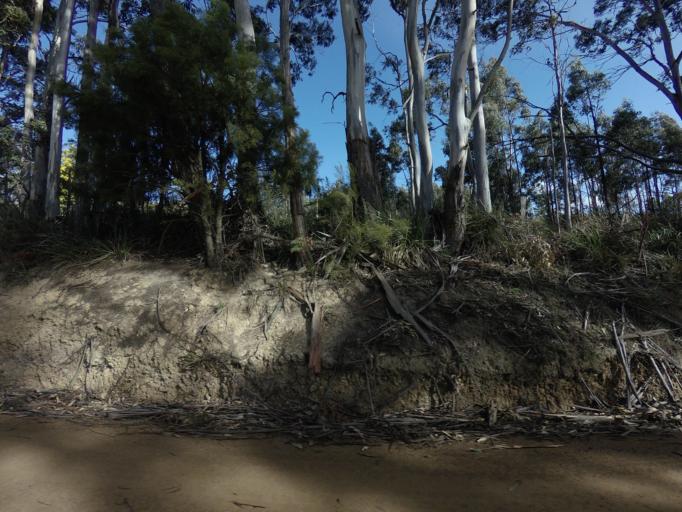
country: AU
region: Tasmania
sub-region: Kingborough
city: Kettering
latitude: -43.0894
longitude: 147.2655
